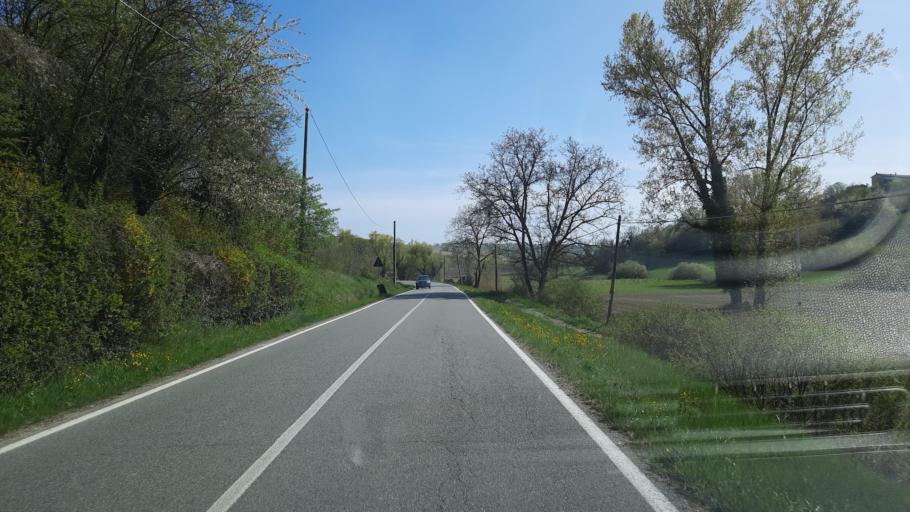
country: IT
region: Piedmont
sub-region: Provincia di Alessandria
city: Ottiglio
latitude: 45.0425
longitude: 8.3476
